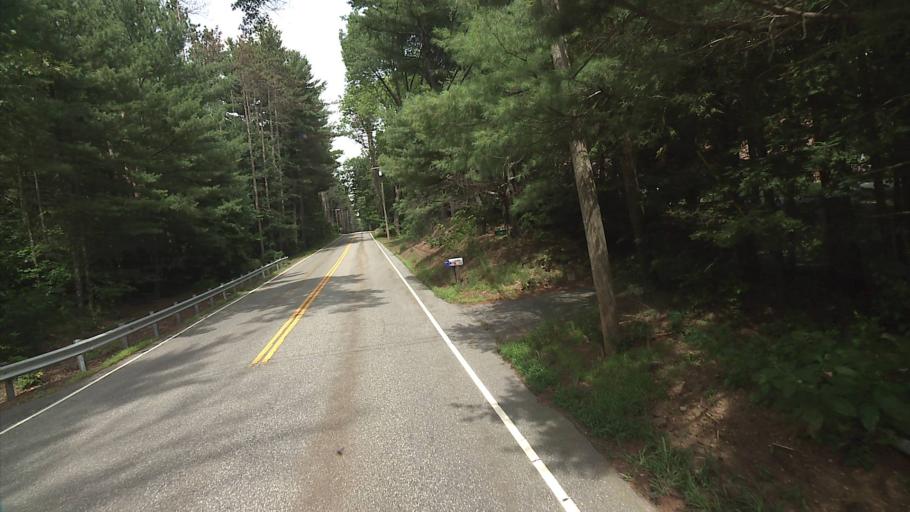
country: US
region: Massachusetts
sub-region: Hampden County
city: Holland
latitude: 42.0065
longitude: -72.1481
